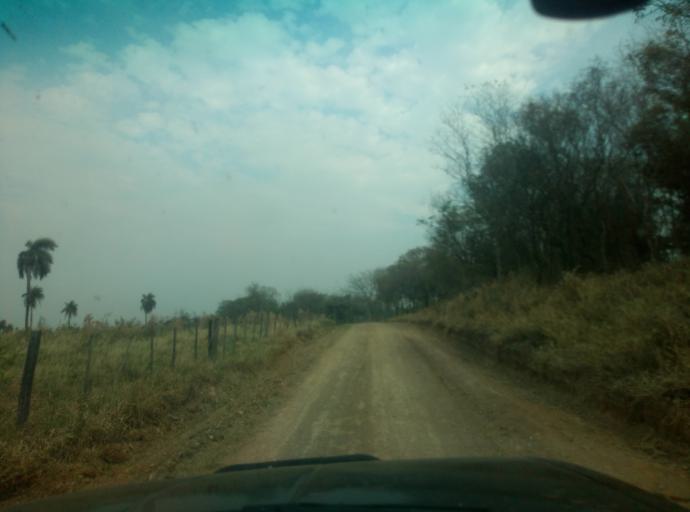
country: PY
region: Caaguazu
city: San Joaquin
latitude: -25.0871
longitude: -56.1428
